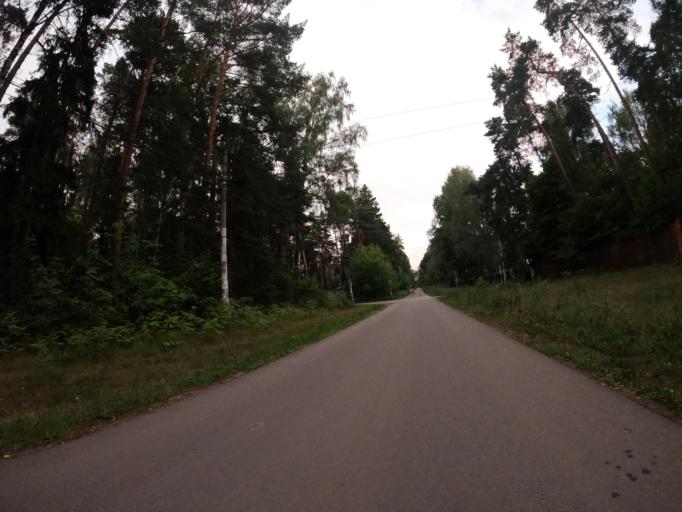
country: RU
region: Moskovskaya
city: Rodniki
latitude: 55.6399
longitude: 38.0676
